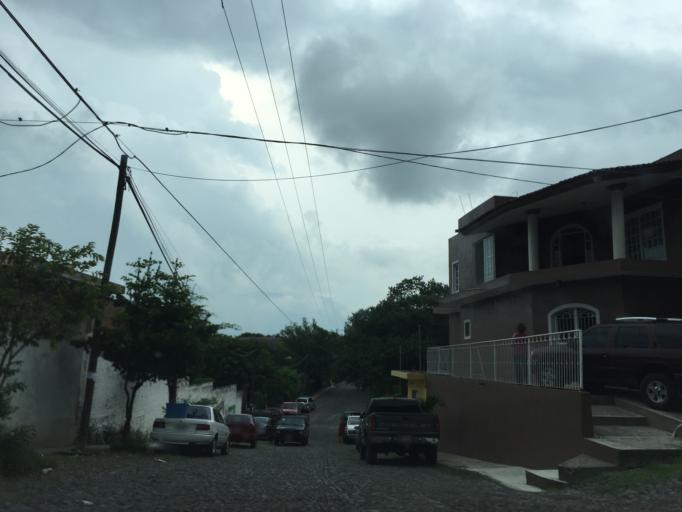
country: MX
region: Colima
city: Comala
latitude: 19.3298
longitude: -103.7614
